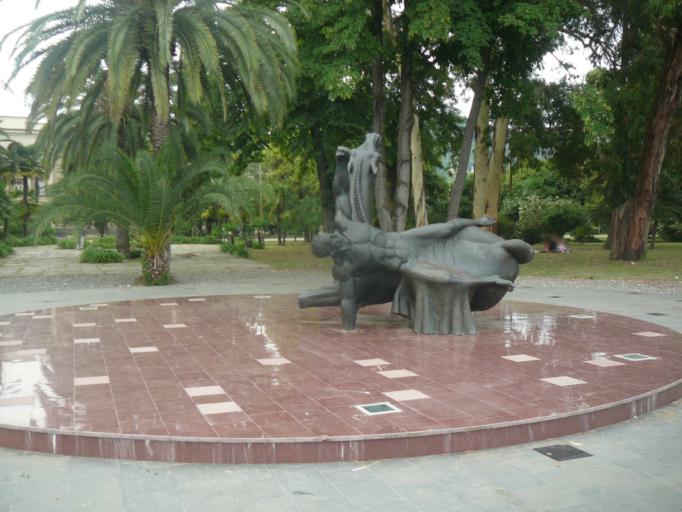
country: GE
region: Abkhazia
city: Sokhumi
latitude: 42.9990
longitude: 41.0284
